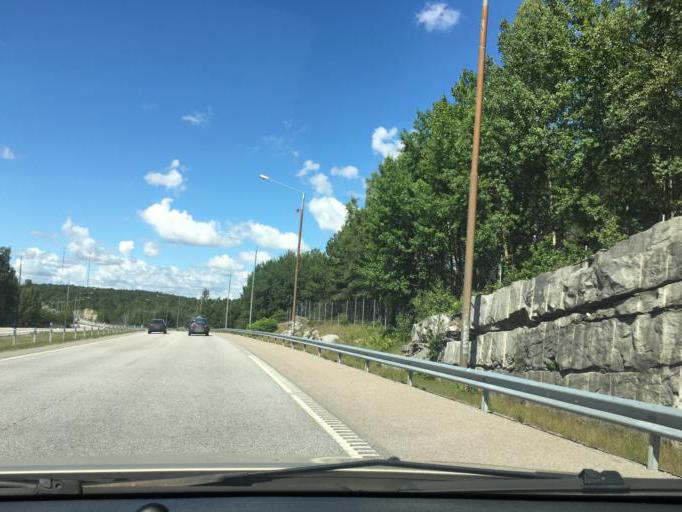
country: SE
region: Stockholm
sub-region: Nacka Kommun
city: Fisksatra
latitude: 59.2919
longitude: 18.2408
